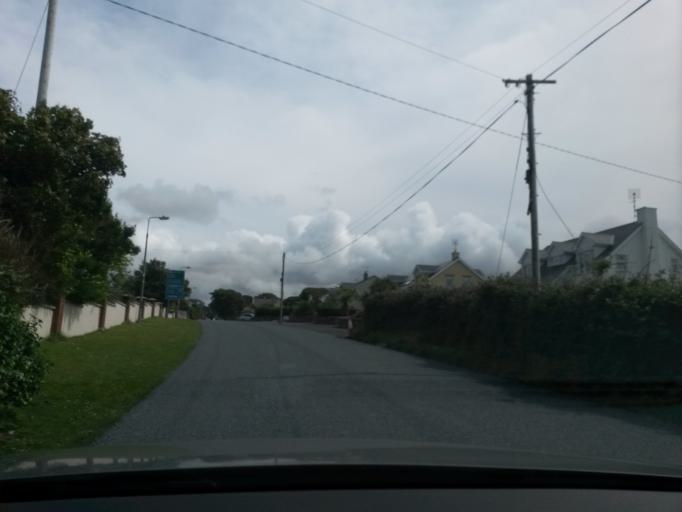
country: IE
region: Connaught
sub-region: Sligo
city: Sligo
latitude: 54.4320
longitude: -8.4562
